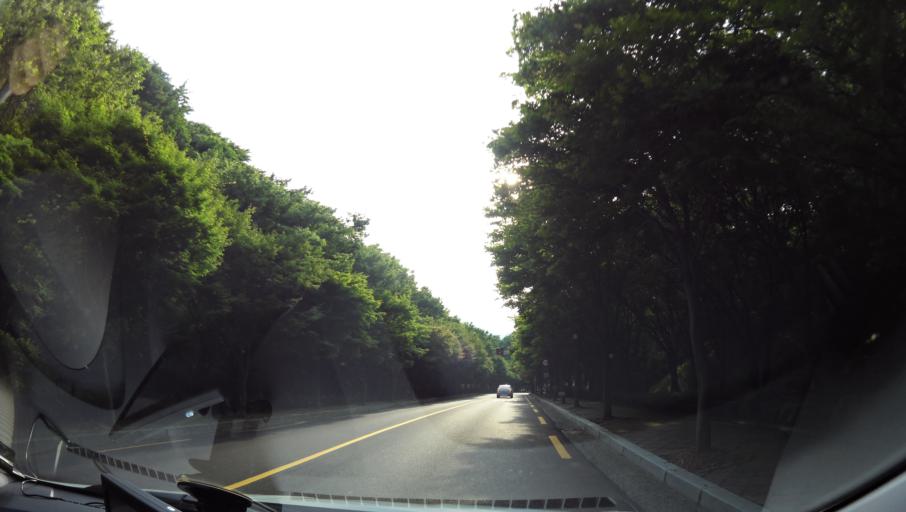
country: KR
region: Daegu
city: Daegu
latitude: 35.9852
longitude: 128.6604
